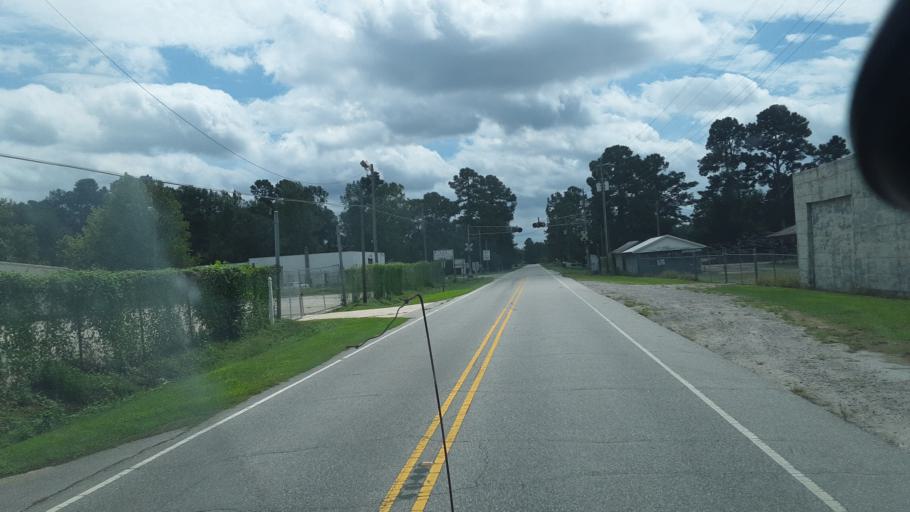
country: US
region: North Carolina
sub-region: Robeson County
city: Fairmont
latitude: 34.2987
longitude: -79.0420
